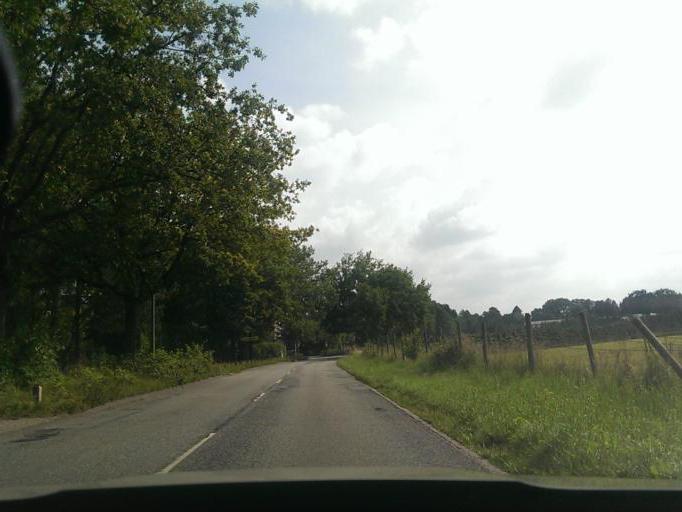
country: DE
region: Hamburg
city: Duvenstedt
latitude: 53.7030
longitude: 10.1037
